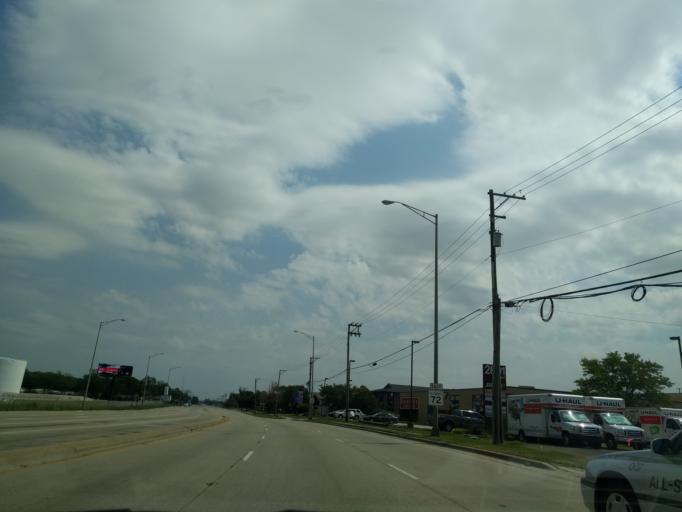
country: US
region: Illinois
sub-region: Cook County
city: Elk Grove Village
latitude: 42.0081
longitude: -87.9398
